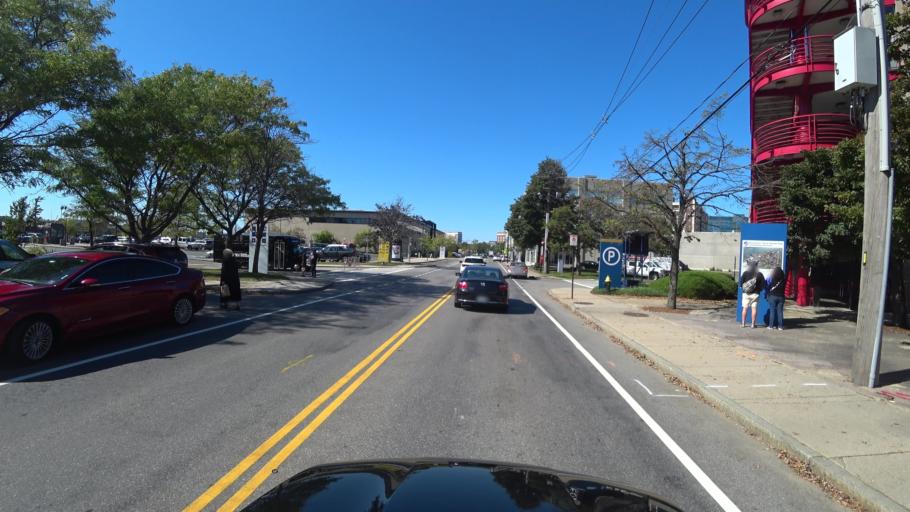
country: US
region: Massachusetts
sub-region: Suffolk County
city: South Boston
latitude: 42.3447
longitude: -71.0340
